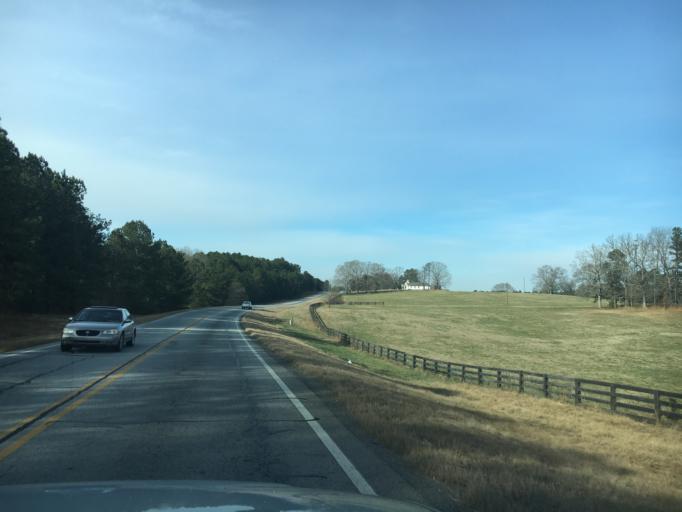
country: US
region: Georgia
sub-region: Jackson County
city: Hoschton
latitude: 34.0771
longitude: -83.7403
